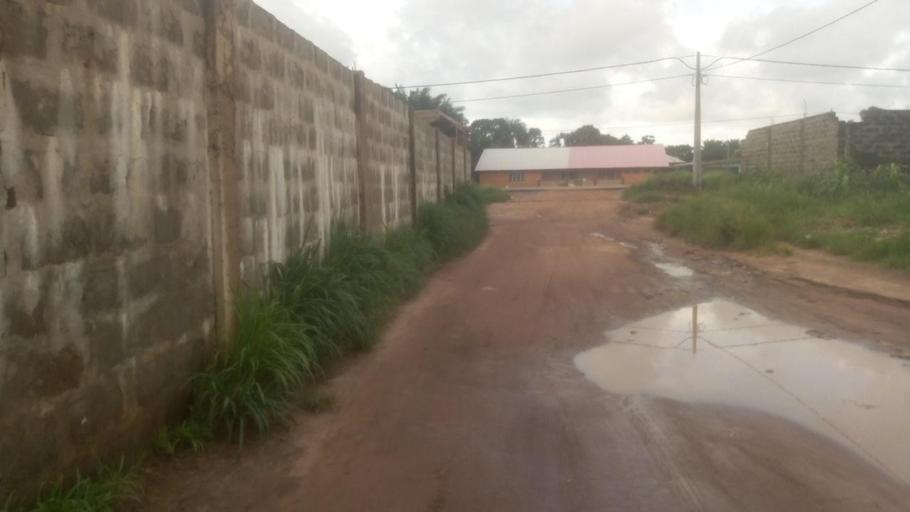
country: SL
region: Northern Province
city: Masoyila
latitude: 8.6073
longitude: -13.1846
